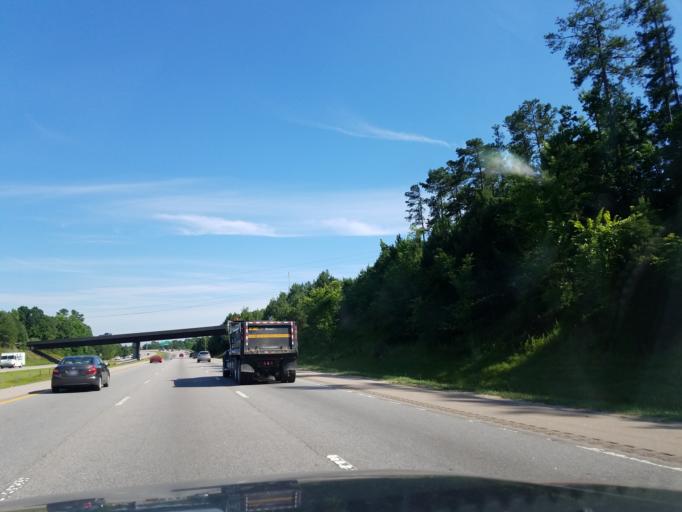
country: US
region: North Carolina
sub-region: Wake County
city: West Raleigh
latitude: 35.8858
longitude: -78.5918
